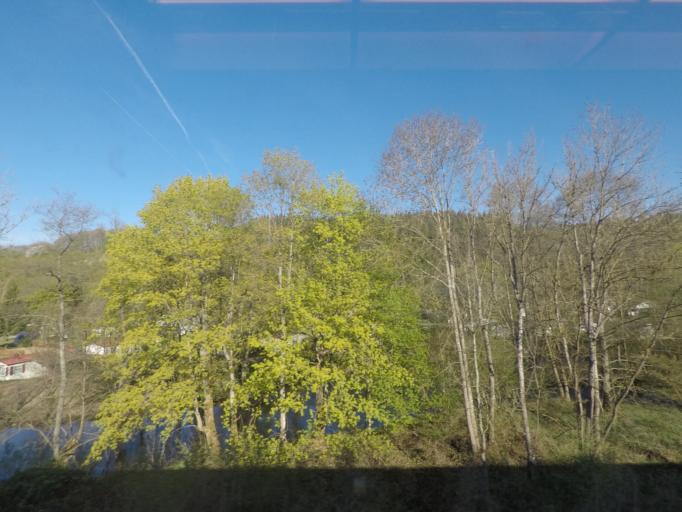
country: BE
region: Wallonia
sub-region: Province du Luxembourg
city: Nassogne
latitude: 50.0970
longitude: 5.2881
